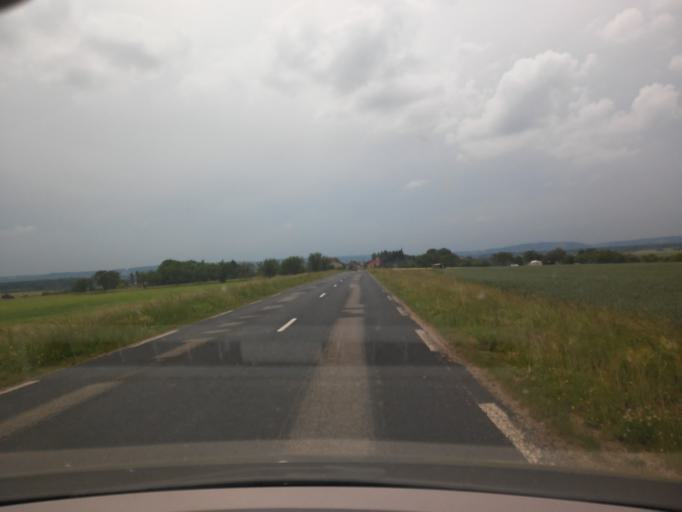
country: FR
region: Lorraine
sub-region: Departement de la Meuse
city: Vigneulles-les-Hattonchatel
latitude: 48.8461
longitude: 5.7678
